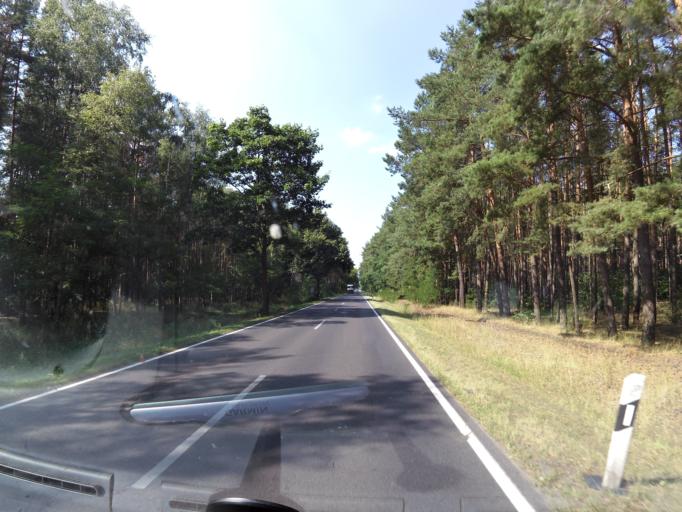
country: DE
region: Brandenburg
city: Zehdenick
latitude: 52.9574
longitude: 13.3752
